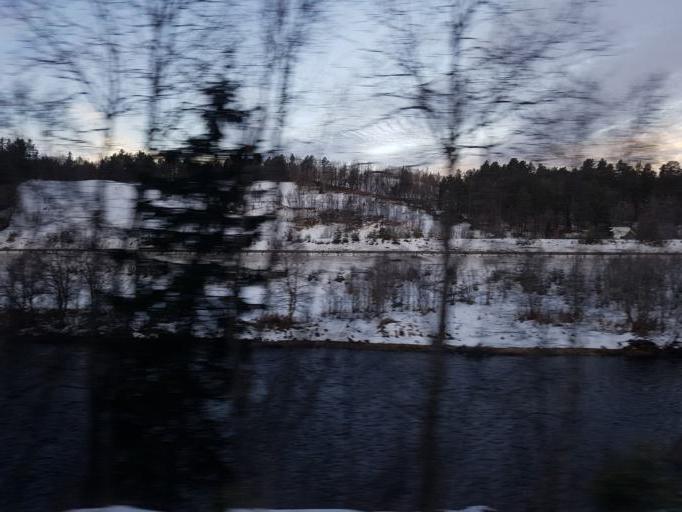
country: NO
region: Sor-Trondelag
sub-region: Rennebu
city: Berkak
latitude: 62.9136
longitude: 10.1387
